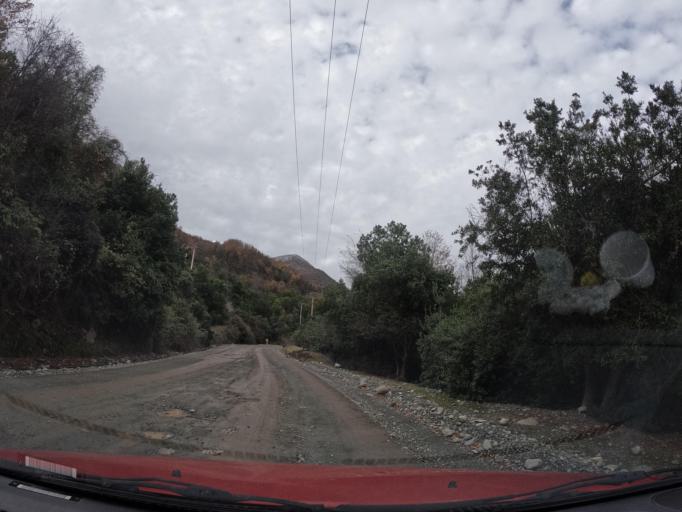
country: CL
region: Maule
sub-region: Provincia de Linares
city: Colbun
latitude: -35.8560
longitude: -71.2053
